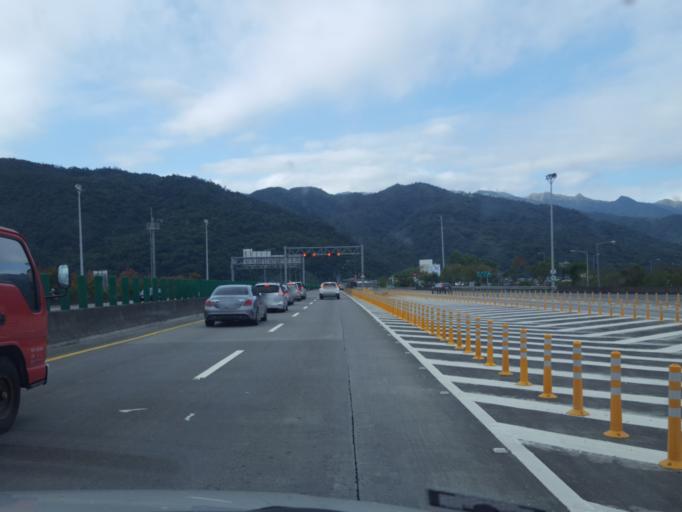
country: TW
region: Taiwan
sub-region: Yilan
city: Yilan
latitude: 24.8345
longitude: 121.7907
